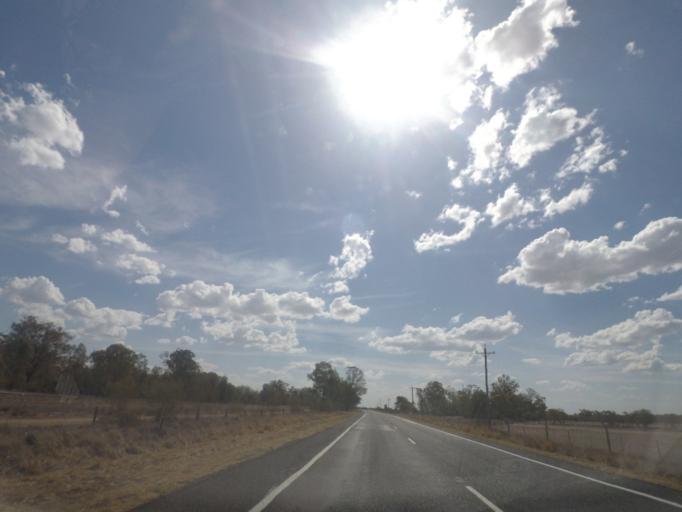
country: AU
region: New South Wales
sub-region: Moree Plains
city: Boggabilla
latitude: -28.4144
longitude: 151.1477
